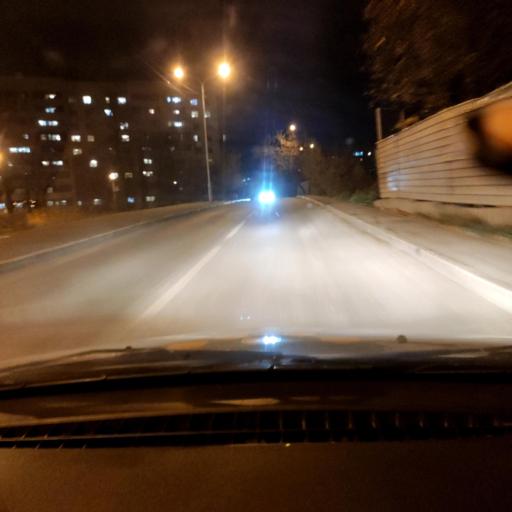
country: RU
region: Bashkortostan
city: Ufa
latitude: 54.7821
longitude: 56.0159
